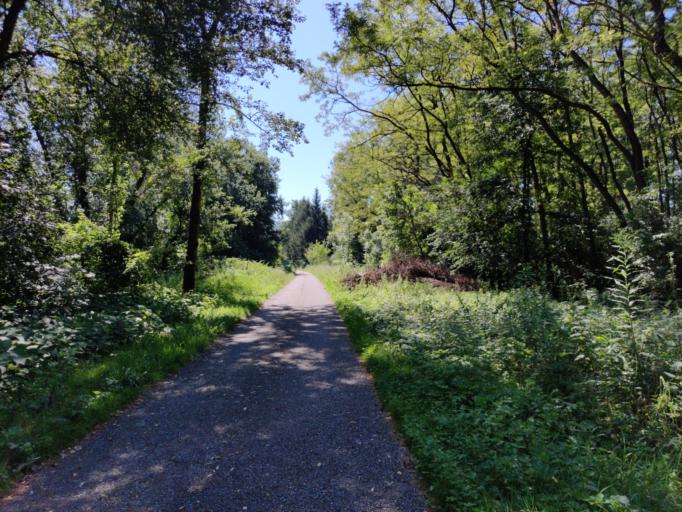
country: AT
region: Styria
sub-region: Politischer Bezirk Leibnitz
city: Wildon
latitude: 46.8988
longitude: 15.4959
